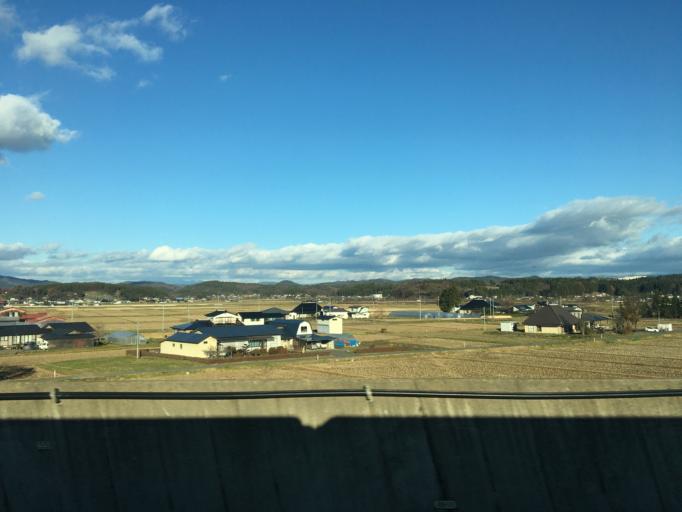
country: JP
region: Iwate
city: Mizusawa
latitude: 39.2019
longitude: 141.1502
